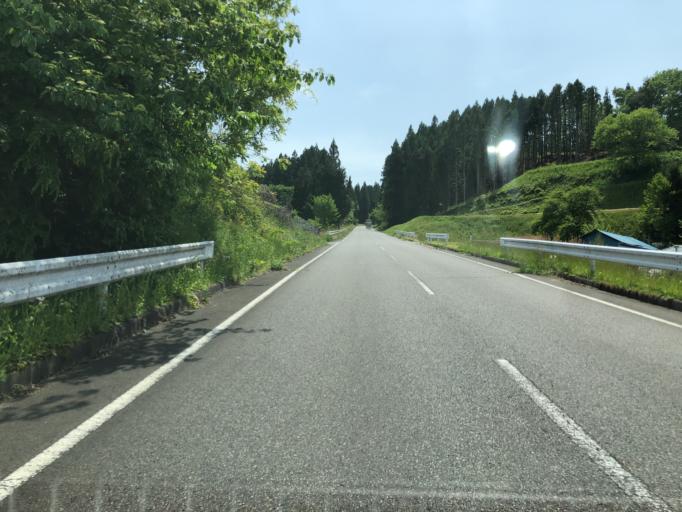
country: JP
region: Fukushima
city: Ishikawa
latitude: 37.1792
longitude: 140.5094
